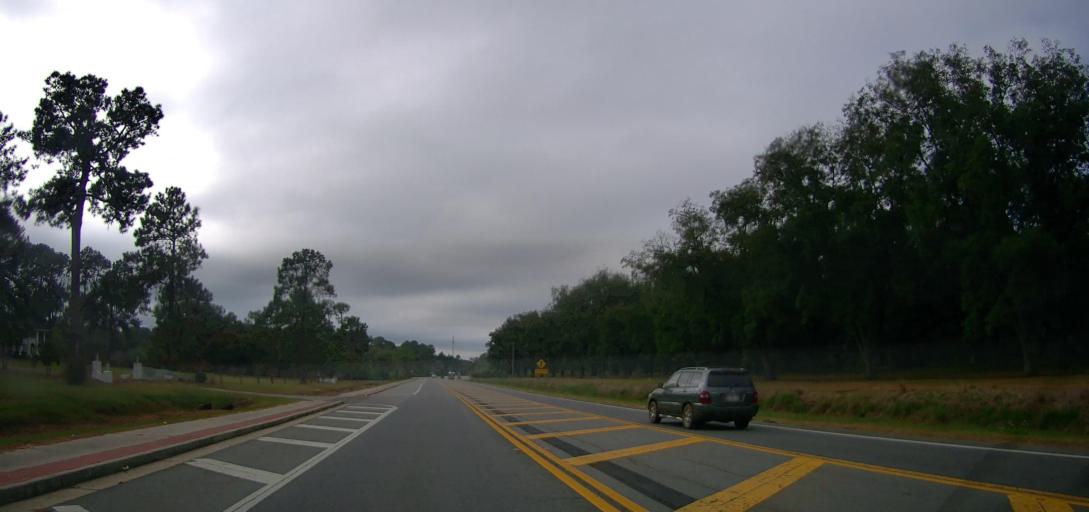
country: US
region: Georgia
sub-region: Tift County
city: Omega
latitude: 31.3354
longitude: -83.6018
